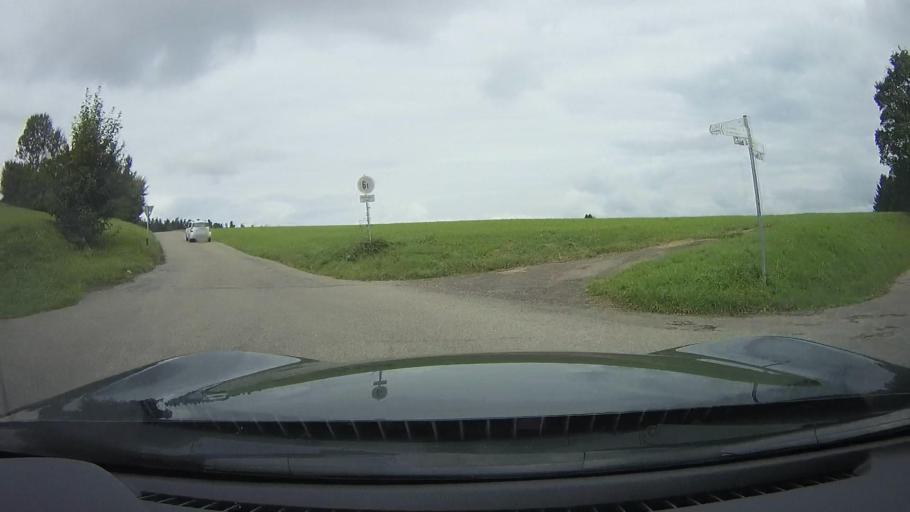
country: DE
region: Baden-Wuerttemberg
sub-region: Regierungsbezirk Stuttgart
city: Althutte
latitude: 48.9243
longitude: 9.5934
